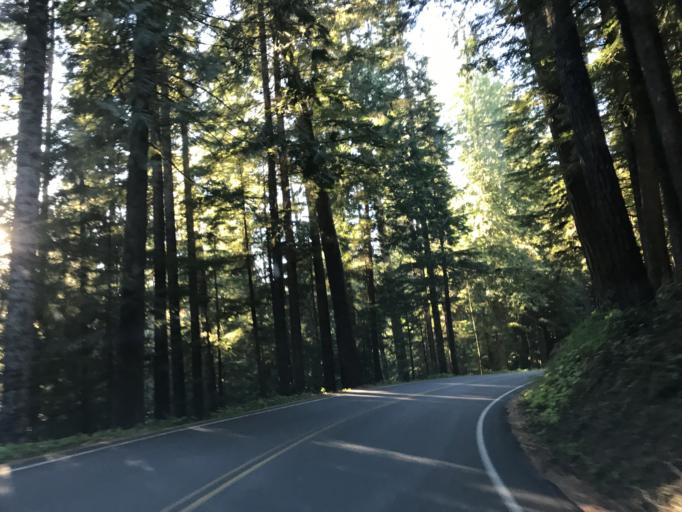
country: US
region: Washington
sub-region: Pierce County
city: Eatonville
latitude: 46.7306
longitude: -121.8332
